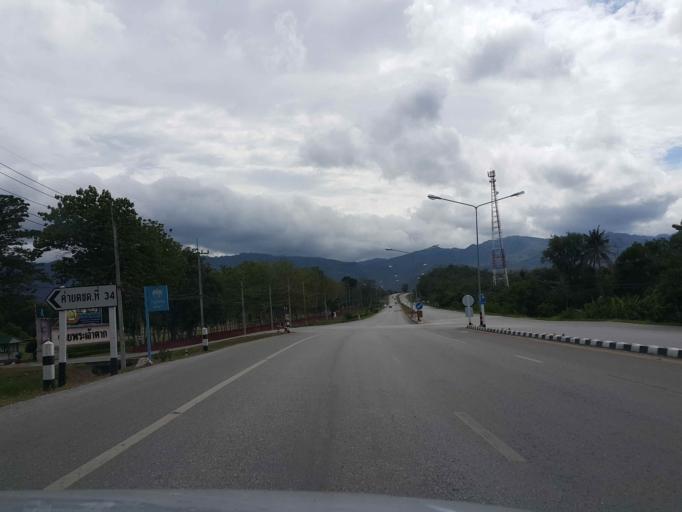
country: TH
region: Tak
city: Tak
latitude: 16.8105
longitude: 99.0598
